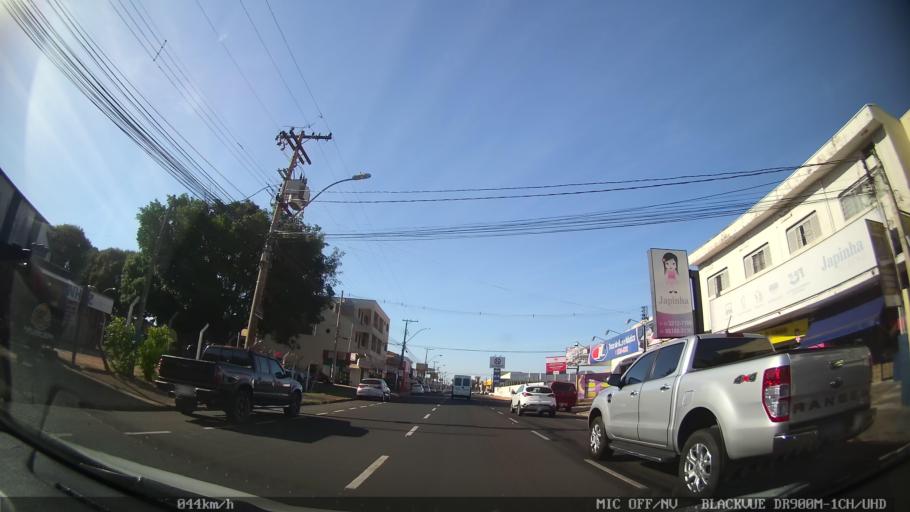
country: BR
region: Sao Paulo
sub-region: Sao Jose Do Rio Preto
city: Sao Jose do Rio Preto
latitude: -20.7954
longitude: -49.3640
